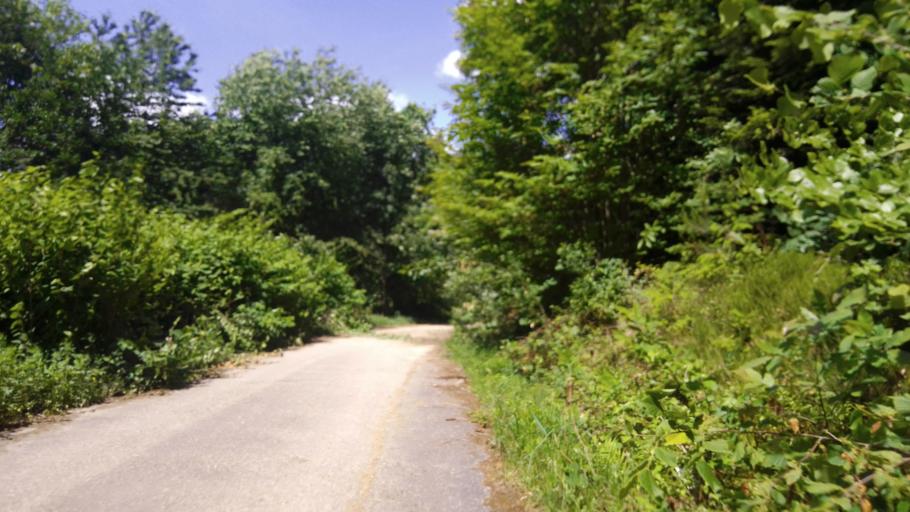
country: DE
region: Baden-Wuerttemberg
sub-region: Karlsruhe Region
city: Sinzheim
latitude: 48.7387
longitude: 8.1954
